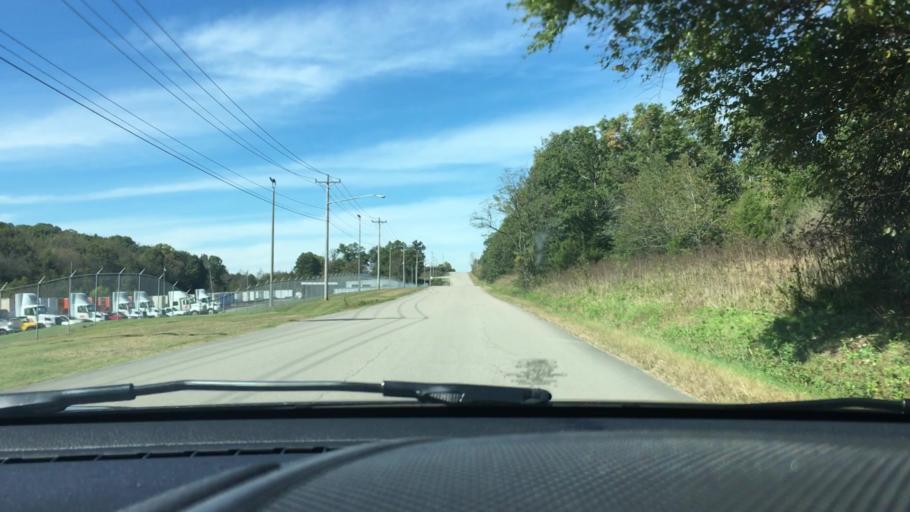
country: US
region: Tennessee
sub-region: Giles County
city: Pulaski
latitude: 35.2190
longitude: -87.0633
